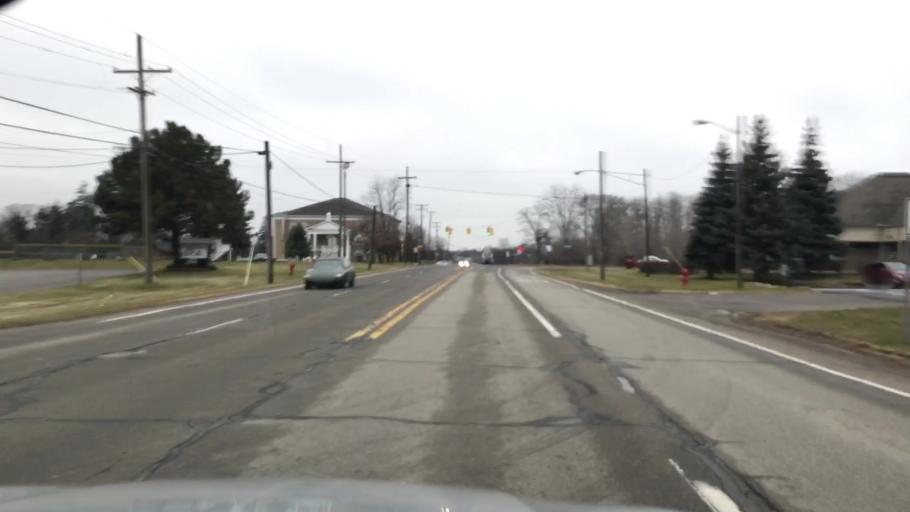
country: US
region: Michigan
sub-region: Wayne County
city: Plymouth
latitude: 42.3751
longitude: -83.4488
